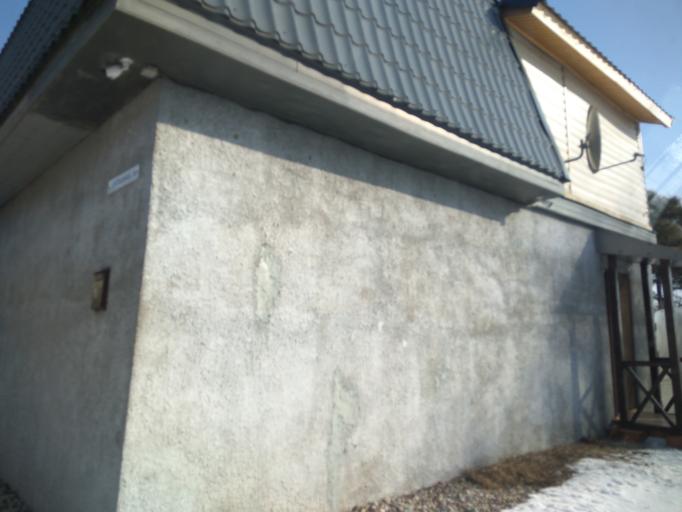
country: RU
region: Kaliningrad
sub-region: Zelenogradskiy Rayon
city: Zelenogradsk
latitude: 55.0134
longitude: 20.6194
